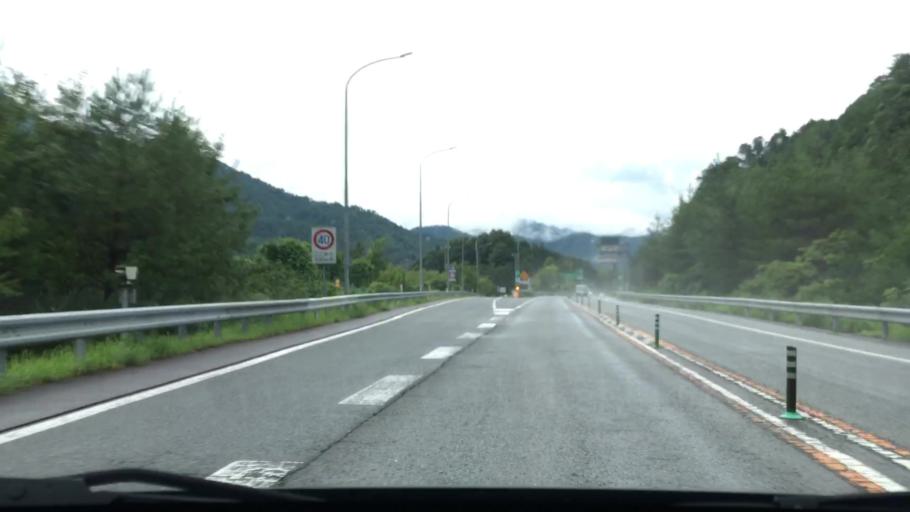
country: JP
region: Hyogo
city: Toyooka
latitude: 35.2972
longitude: 134.8254
